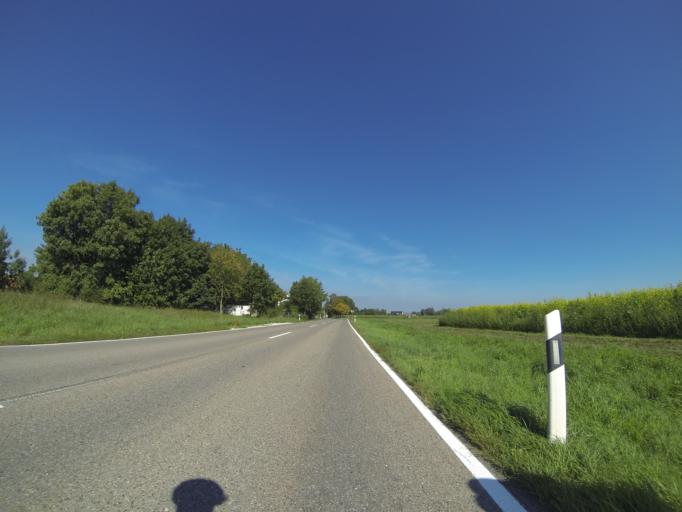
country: DE
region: Baden-Wuerttemberg
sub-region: Tuebingen Region
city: Erbach
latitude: 48.3227
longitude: 9.9245
